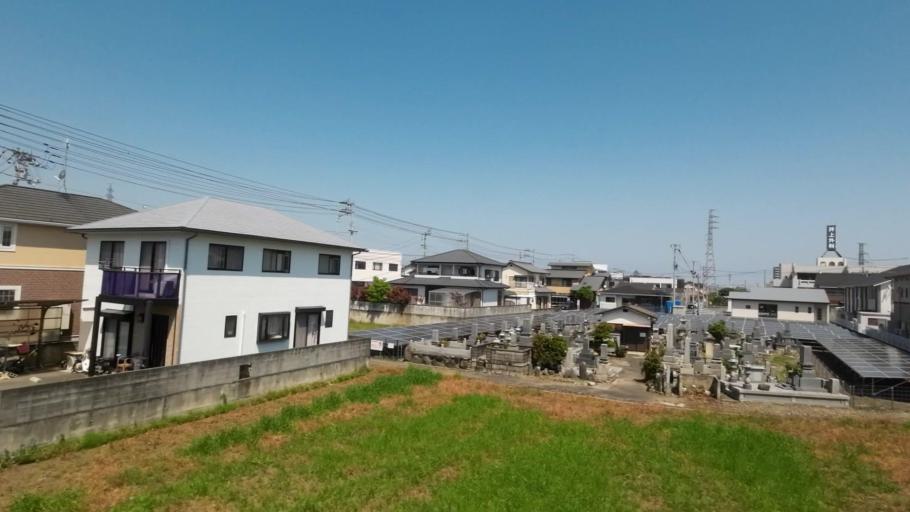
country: JP
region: Ehime
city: Niihama
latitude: 33.9435
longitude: 133.2896
